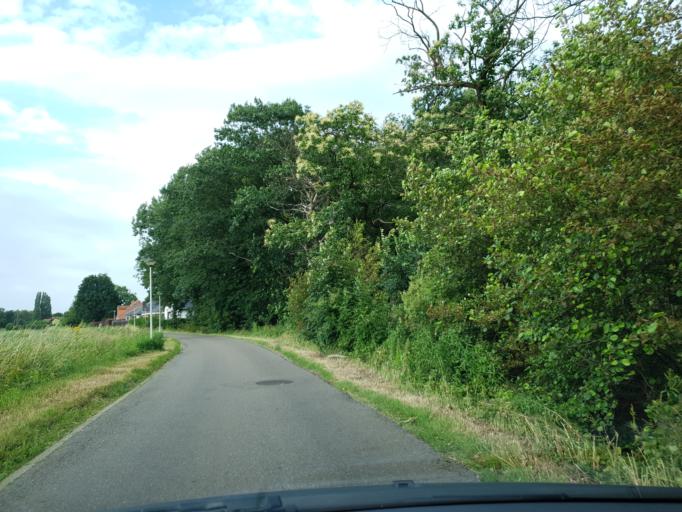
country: BE
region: Flanders
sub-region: Provincie Antwerpen
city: Kapellen
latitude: 51.2719
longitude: 4.4452
